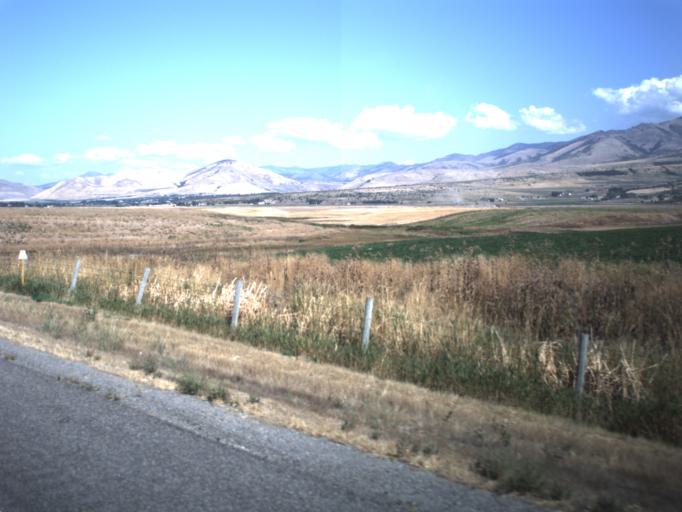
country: US
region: Utah
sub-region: Cache County
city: Lewiston
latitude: 41.9771
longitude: -111.8128
